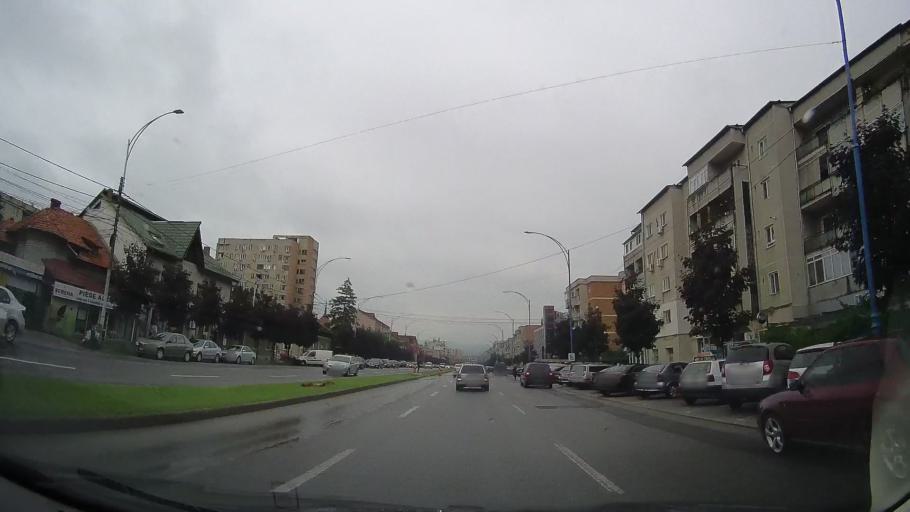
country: RO
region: Mehedinti
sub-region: Municipiul Drobeta-Turnu Severin
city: Drobeta-Turnu Severin
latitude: 44.6327
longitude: 22.6592
